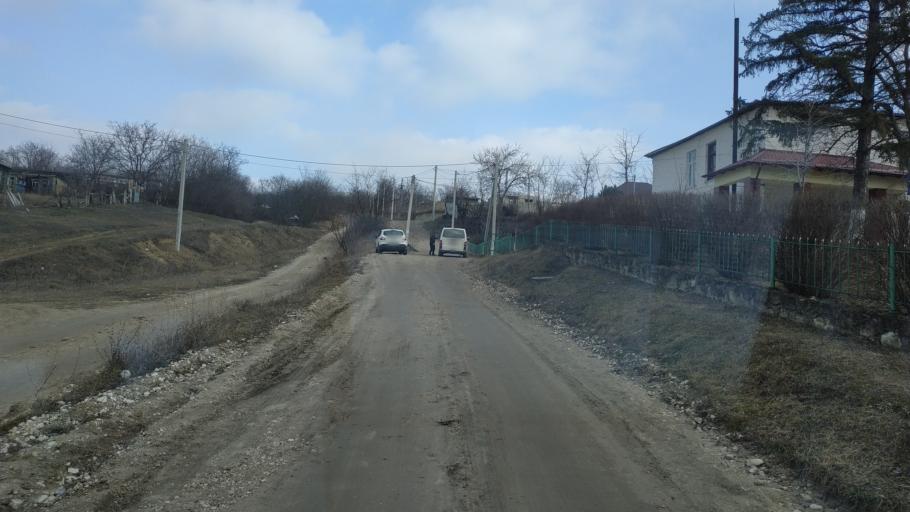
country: MD
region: Nisporeni
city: Nisporeni
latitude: 46.9434
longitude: 28.3245
